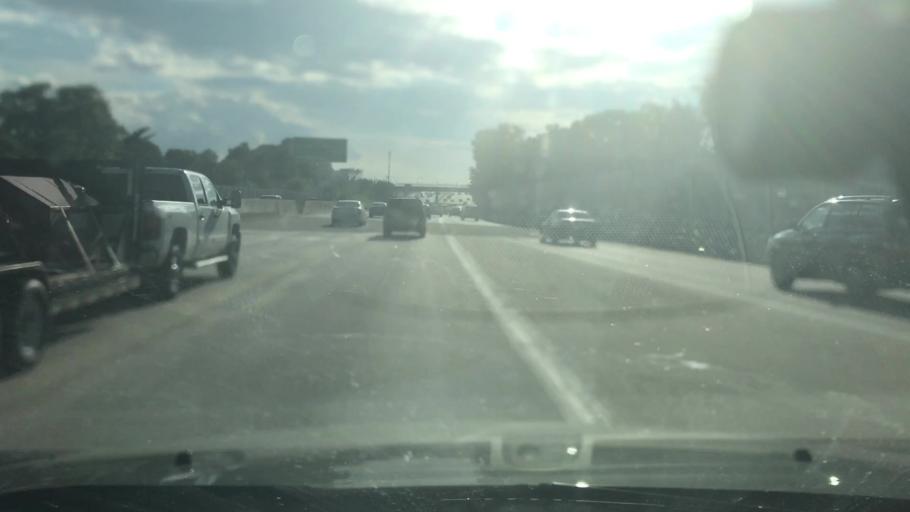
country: US
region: Missouri
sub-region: Saint Louis County
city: Richmond Heights
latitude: 38.6302
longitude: -90.3229
